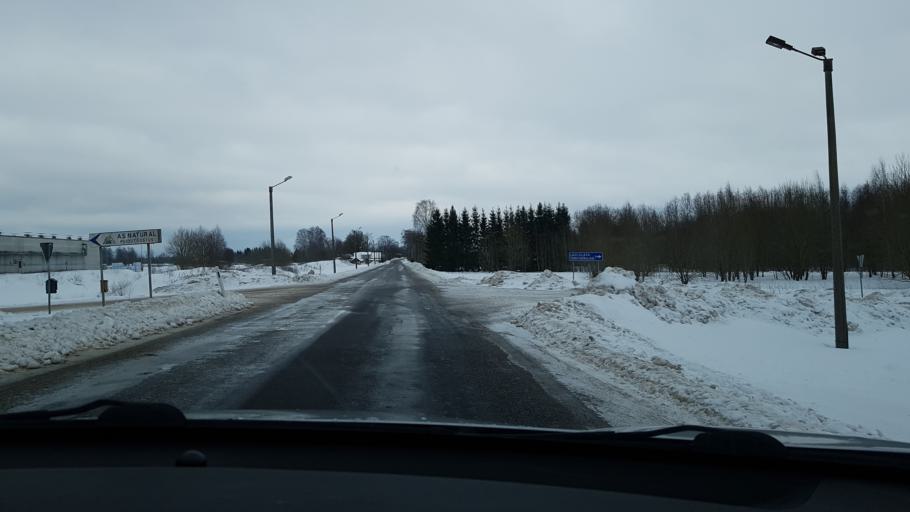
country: EE
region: Jaervamaa
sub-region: Koeru vald
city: Koeru
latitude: 58.9704
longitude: 26.0150
